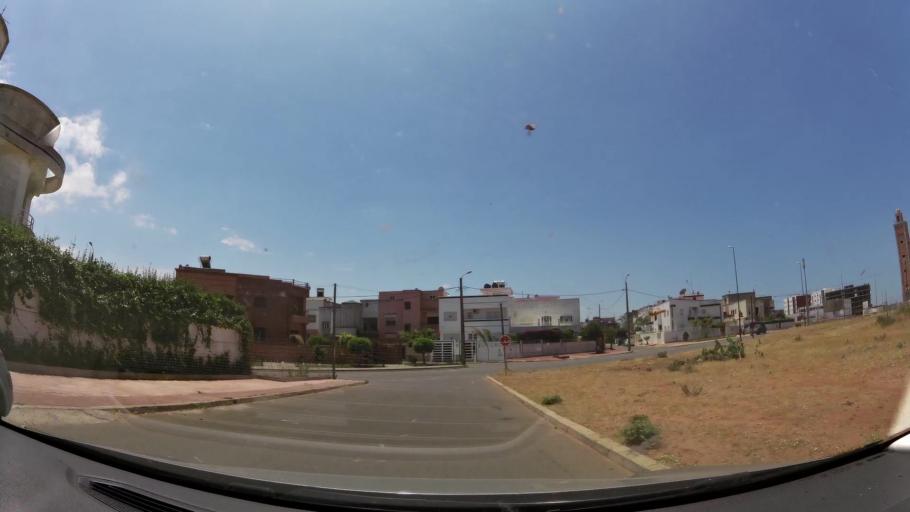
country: MA
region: Gharb-Chrarda-Beni Hssen
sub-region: Kenitra Province
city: Kenitra
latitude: 34.2658
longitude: -6.6214
